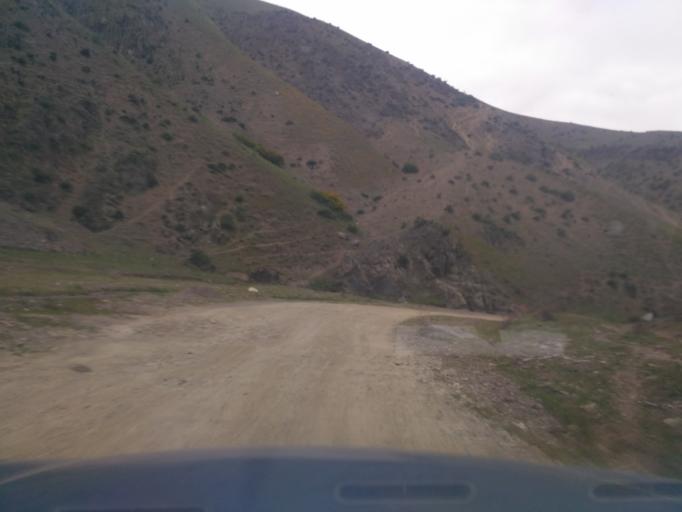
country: UZ
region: Jizzax
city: Zomin
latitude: 39.8547
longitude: 68.3898
